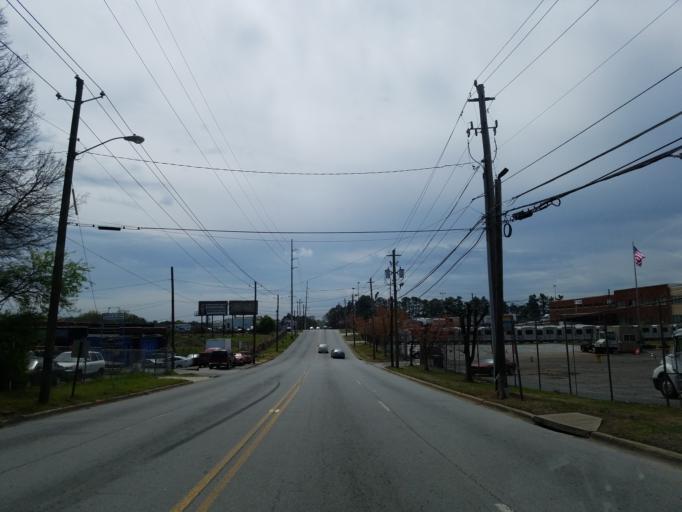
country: US
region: Georgia
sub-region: Fulton County
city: East Point
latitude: 33.6941
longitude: -84.4184
